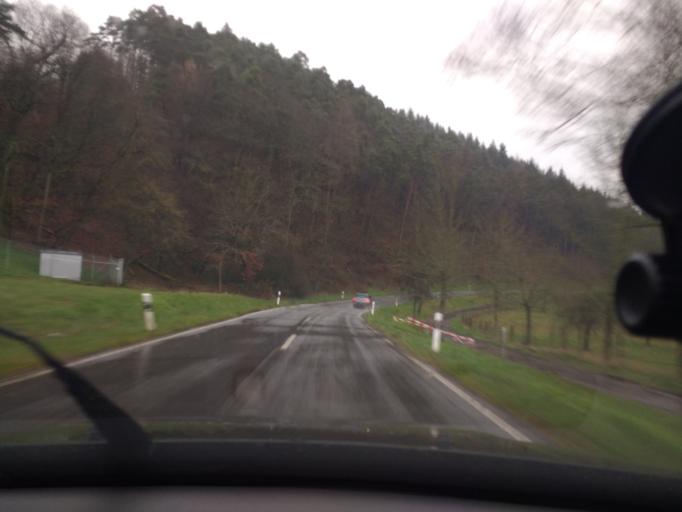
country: DE
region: Rheinland-Pfalz
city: Wawern
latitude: 49.6550
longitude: 6.5329
